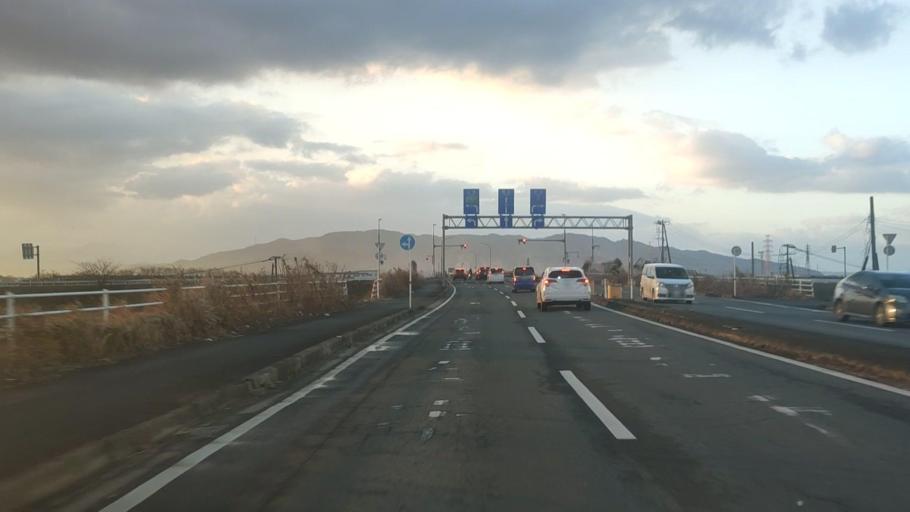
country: JP
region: Kumamoto
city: Uto
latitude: 32.7390
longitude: 130.7047
